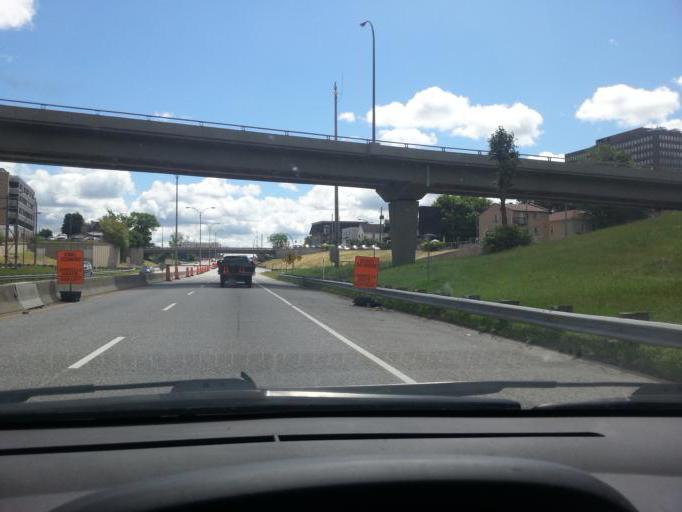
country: CA
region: Ontario
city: Ottawa
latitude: 45.4390
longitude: -75.7113
